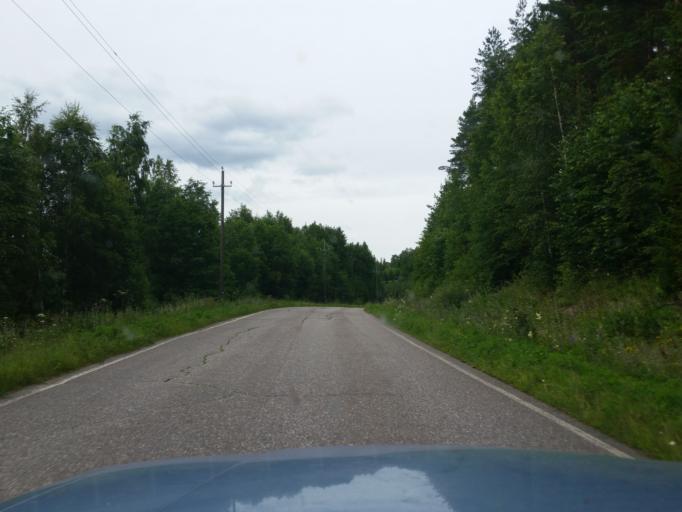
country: FI
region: Uusimaa
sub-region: Helsinki
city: Sammatti
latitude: 60.3940
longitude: 23.8144
